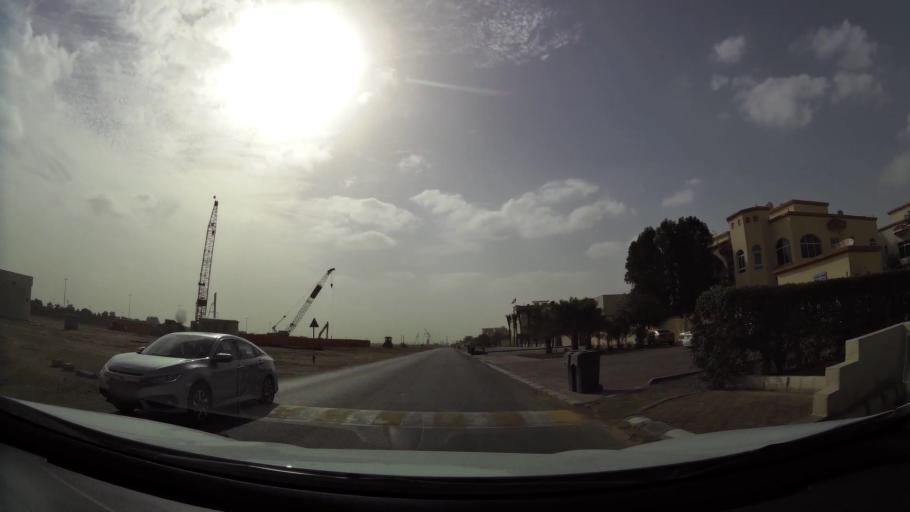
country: AE
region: Abu Dhabi
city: Abu Dhabi
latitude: 24.4045
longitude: 54.5935
